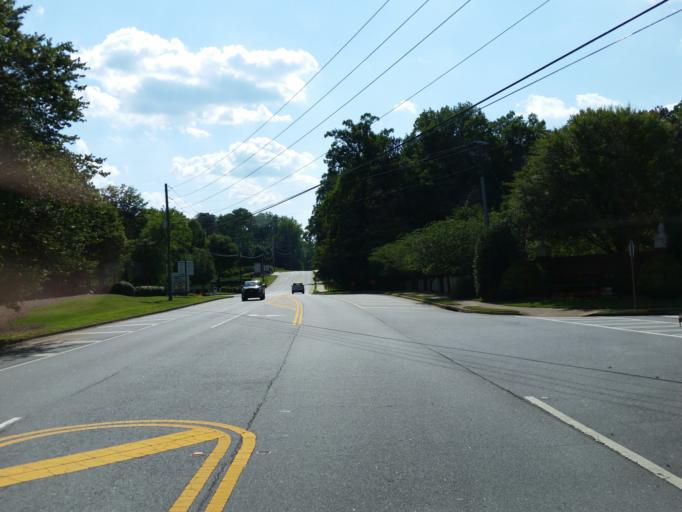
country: US
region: Georgia
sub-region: Cobb County
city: Marietta
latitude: 33.9833
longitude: -84.5008
